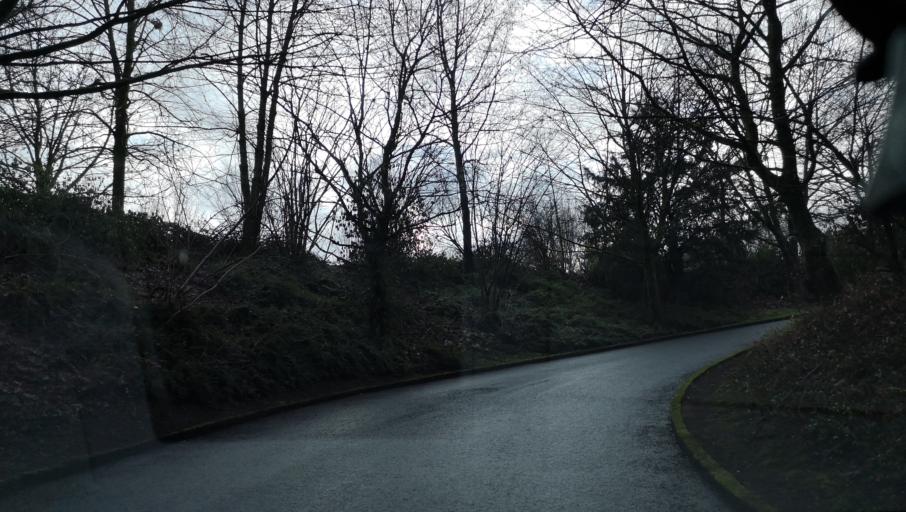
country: DE
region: North Rhine-Westphalia
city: Radevormwald
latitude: 51.1983
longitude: 7.3094
